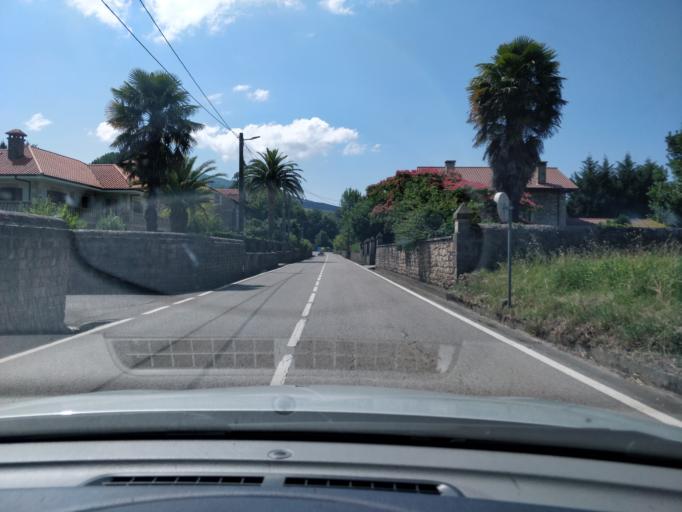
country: ES
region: Cantabria
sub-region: Provincia de Cantabria
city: Corvera
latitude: 43.2724
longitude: -3.9348
